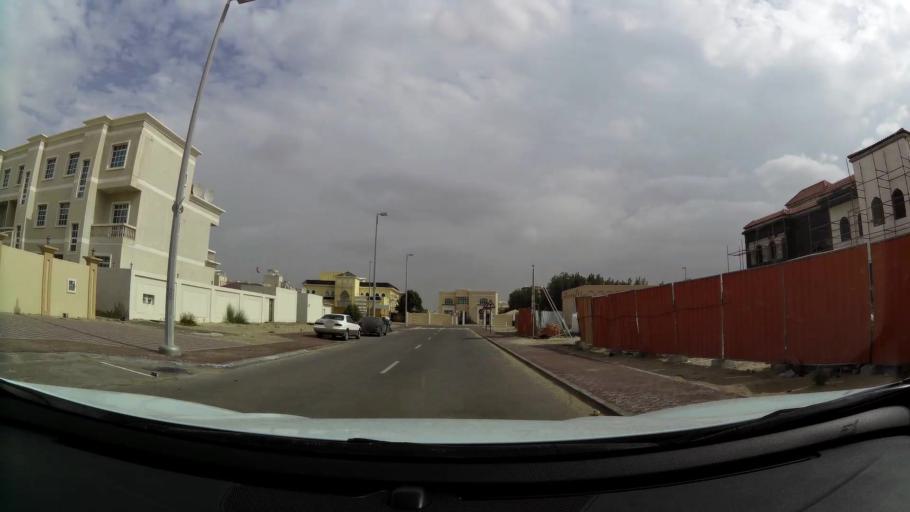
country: AE
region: Abu Dhabi
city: Abu Dhabi
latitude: 24.3817
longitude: 54.6462
